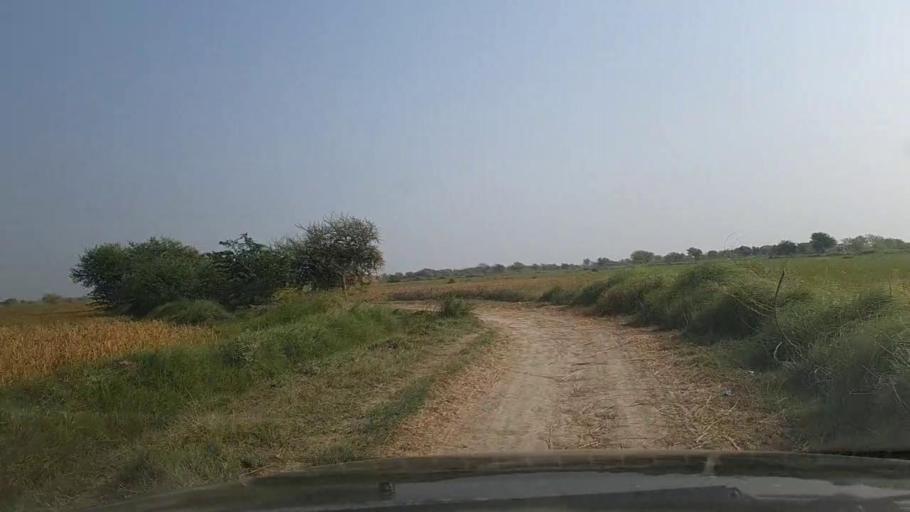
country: PK
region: Sindh
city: Mirpur Batoro
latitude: 24.6795
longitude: 68.2395
